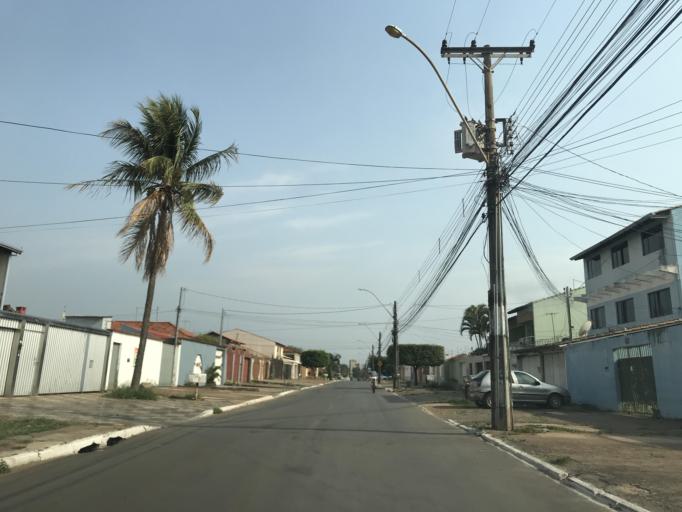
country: BR
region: Federal District
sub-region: Brasilia
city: Brasilia
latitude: -15.8057
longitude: -48.0623
